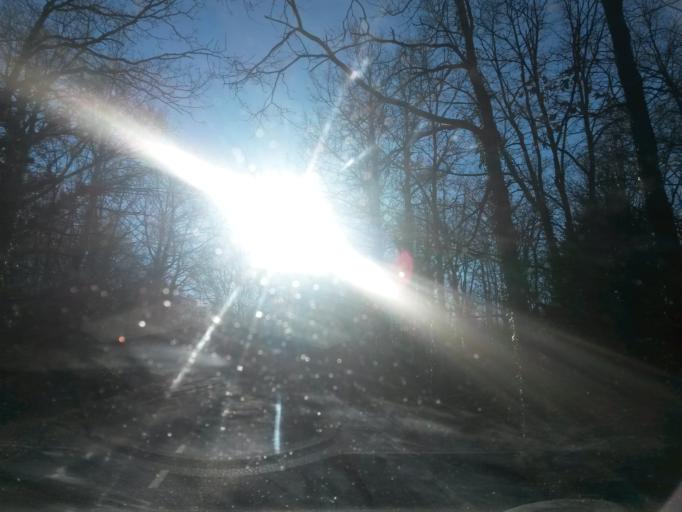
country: ES
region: Catalonia
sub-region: Provincia de Girona
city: les Planes d'Hostoles
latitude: 42.0262
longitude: 2.5339
